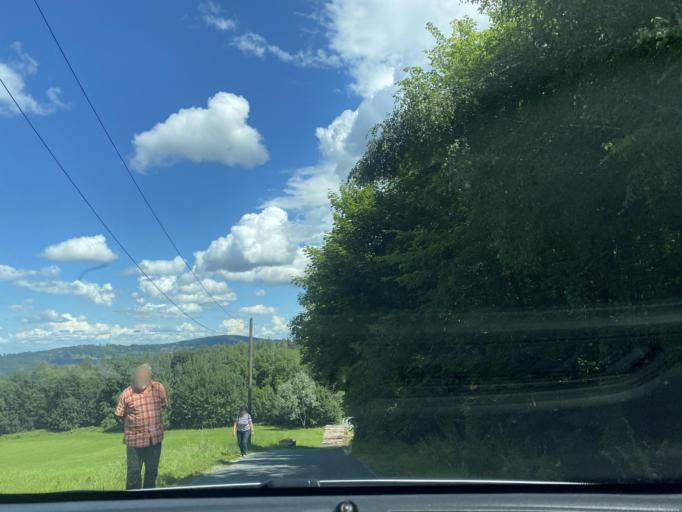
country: DE
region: Saxony
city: Beiersdorf
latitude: 51.0802
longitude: 14.5247
